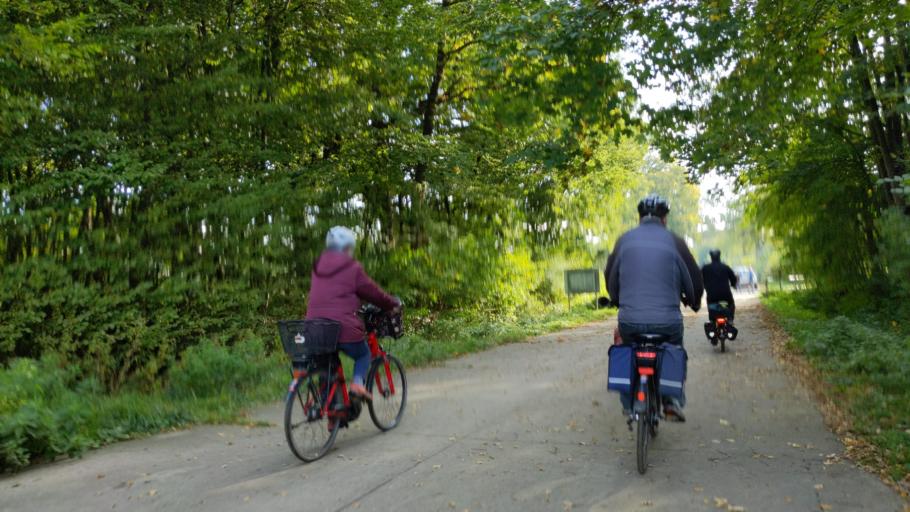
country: DE
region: Schleswig-Holstein
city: Badendorf
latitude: 53.8748
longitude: 10.5863
